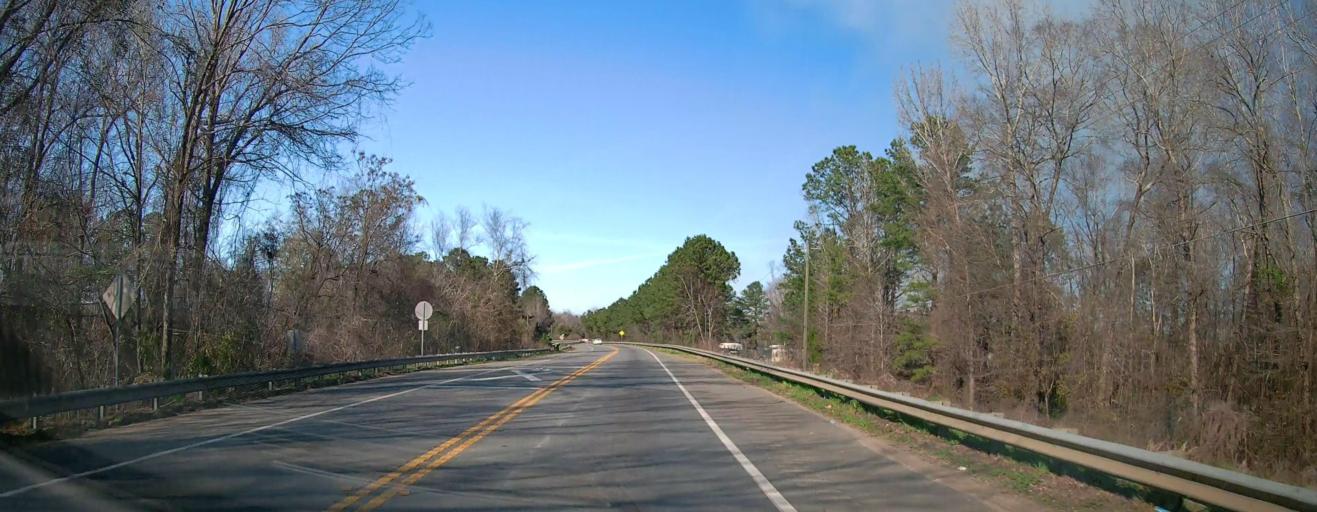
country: US
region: Georgia
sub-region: Macon County
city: Oglethorpe
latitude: 32.3117
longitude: -84.0650
